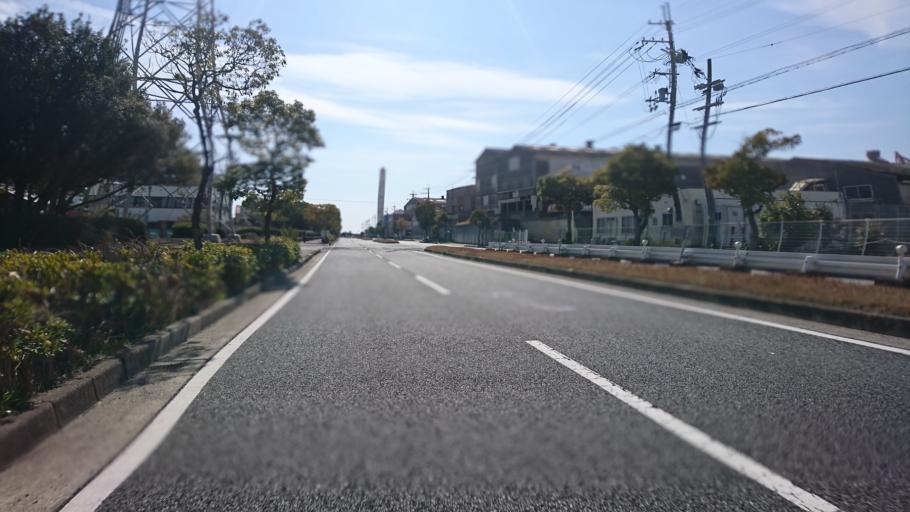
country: JP
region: Hyogo
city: Kakogawacho-honmachi
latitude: 34.6992
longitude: 134.8518
